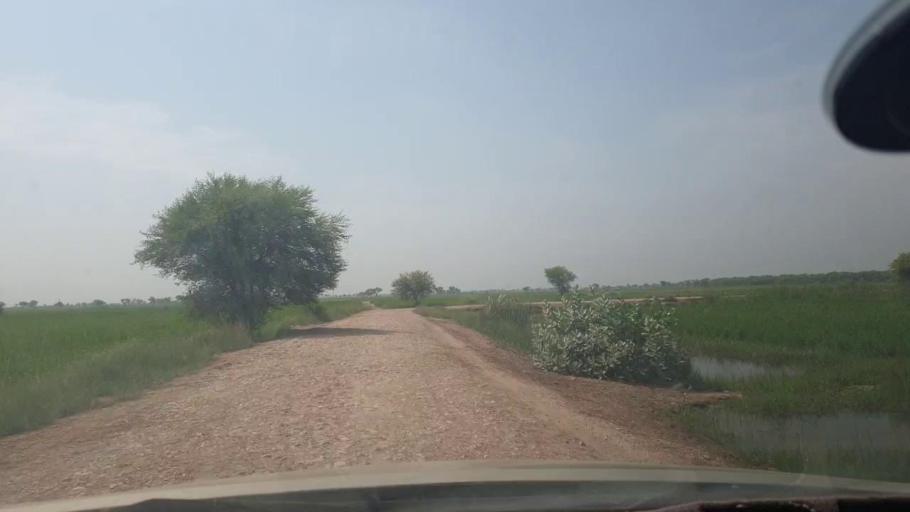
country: PK
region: Sindh
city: Jacobabad
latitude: 28.2654
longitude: 68.5111
